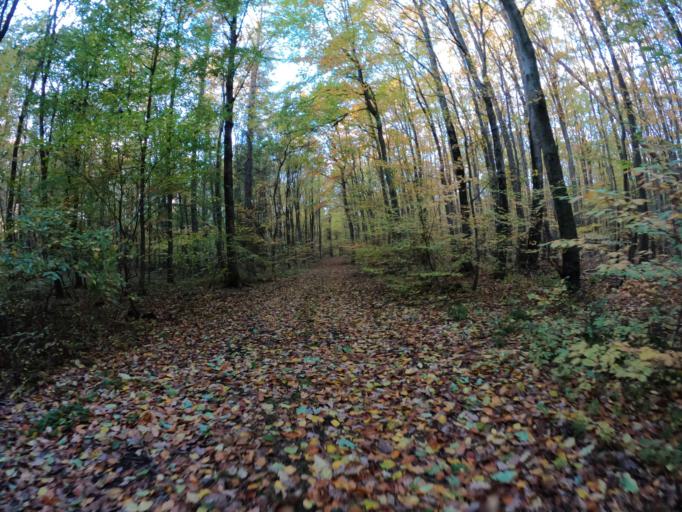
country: PL
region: West Pomeranian Voivodeship
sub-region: Powiat mysliborski
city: Barlinek
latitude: 52.9645
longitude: 15.2335
